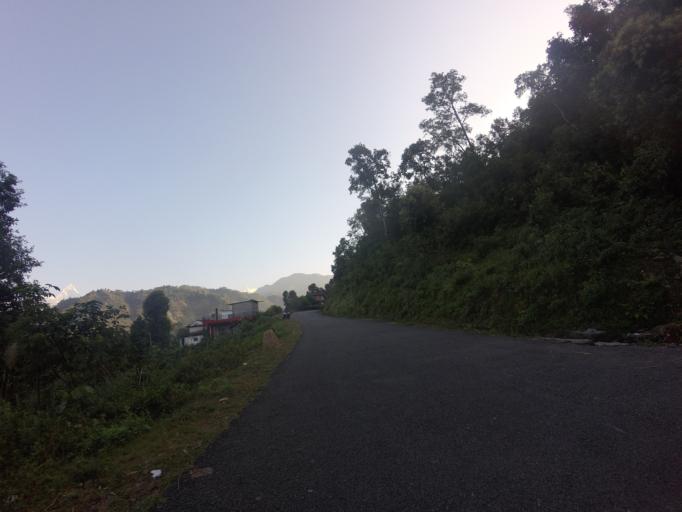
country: NP
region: Western Region
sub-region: Gandaki Zone
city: Pokhara
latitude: 28.2443
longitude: 84.0015
